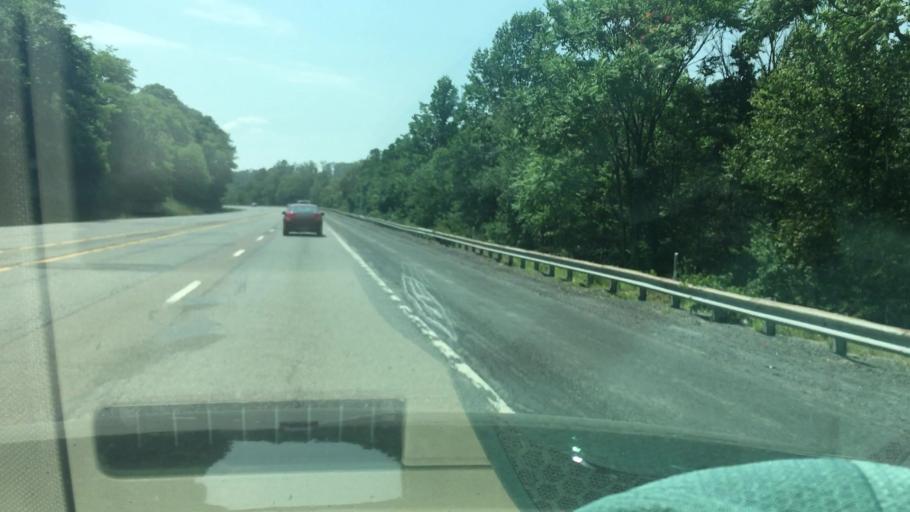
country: US
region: Pennsylvania
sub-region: Schuylkill County
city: Tamaqua
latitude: 40.7695
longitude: -75.9559
